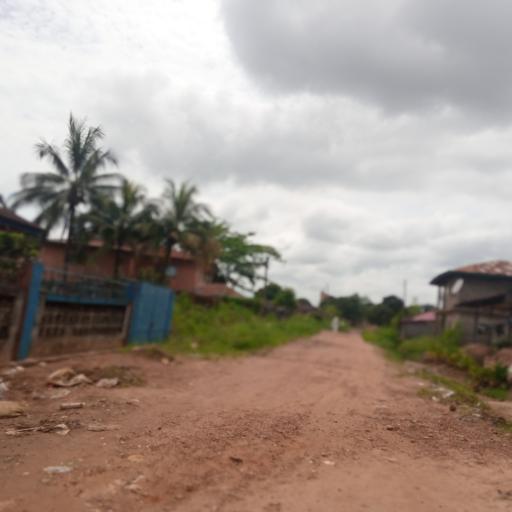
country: SL
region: Eastern Province
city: Kenema
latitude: 7.8861
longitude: -11.1894
